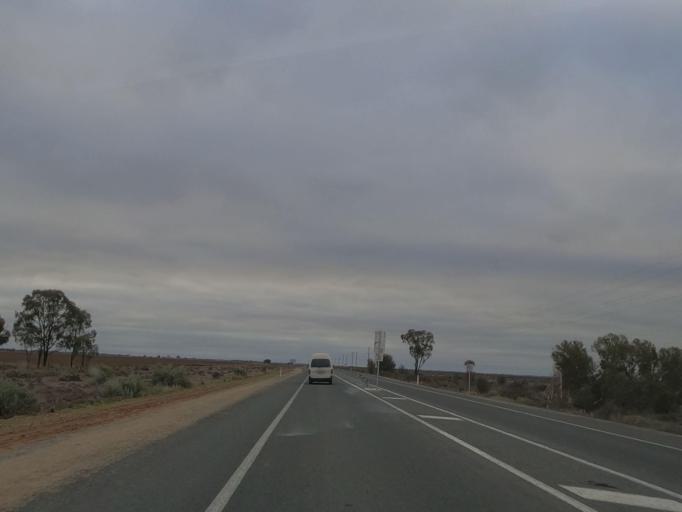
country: AU
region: Victoria
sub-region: Swan Hill
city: Swan Hill
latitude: -35.5176
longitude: 143.7292
